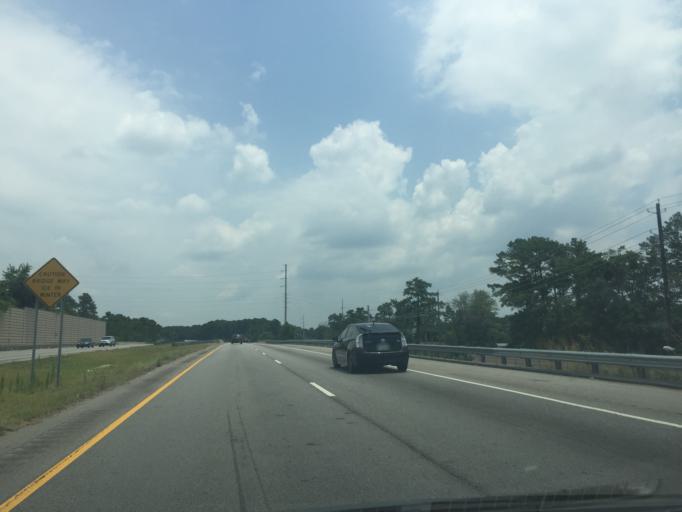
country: US
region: Georgia
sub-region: Chatham County
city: Isle of Hope
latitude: 31.9989
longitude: -81.0799
